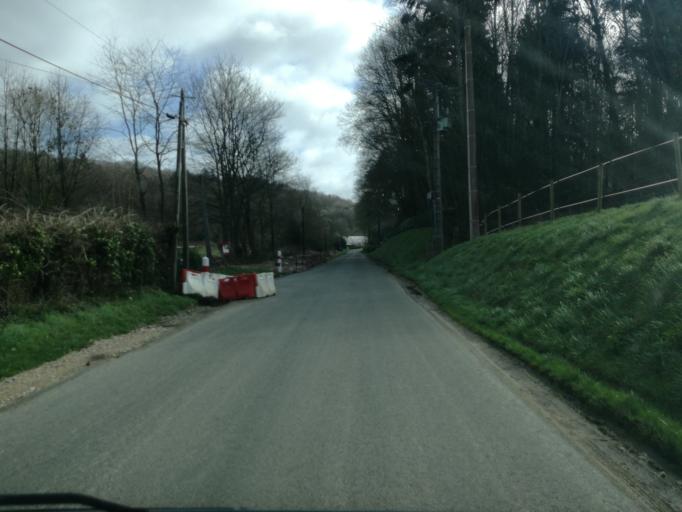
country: FR
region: Haute-Normandie
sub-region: Departement de la Seine-Maritime
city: Bretteville-du-Grand-Caux
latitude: 49.7006
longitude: 0.4550
